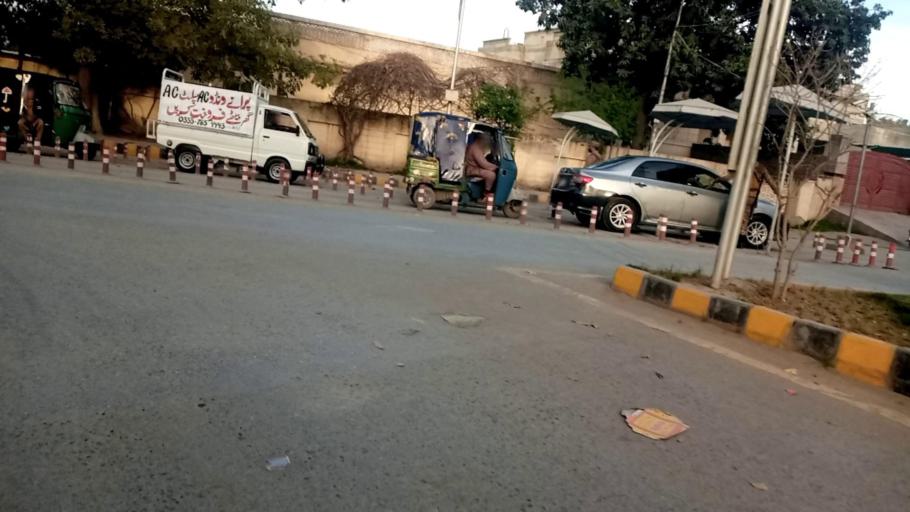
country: PK
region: Khyber Pakhtunkhwa
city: Peshawar
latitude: 34.0197
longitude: 71.5536
